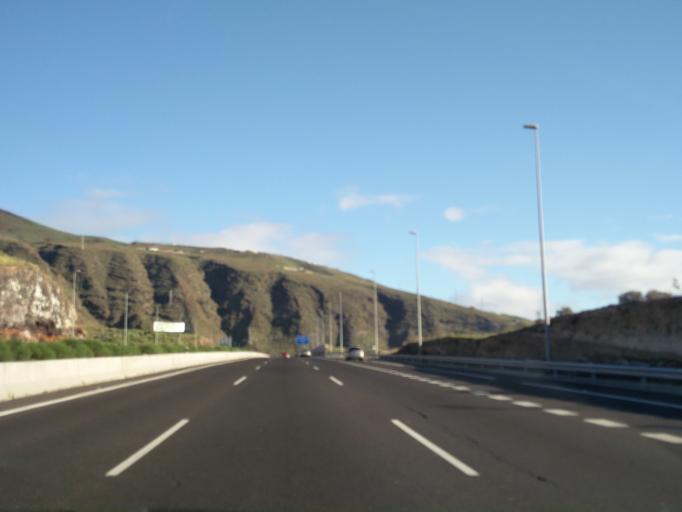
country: ES
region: Canary Islands
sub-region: Provincia de Santa Cruz de Tenerife
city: Candelaria
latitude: 28.3739
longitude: -16.3662
